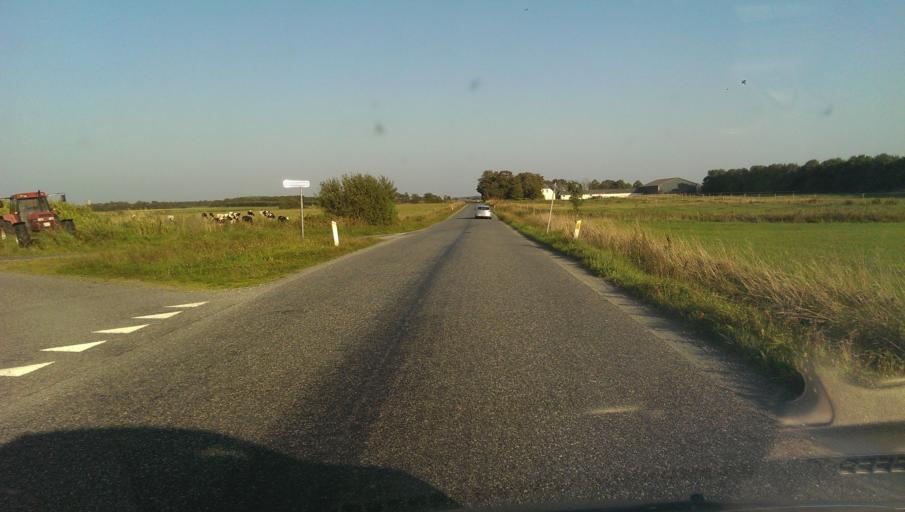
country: DK
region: South Denmark
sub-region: Vejen Kommune
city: Holsted
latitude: 55.4702
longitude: 8.8229
